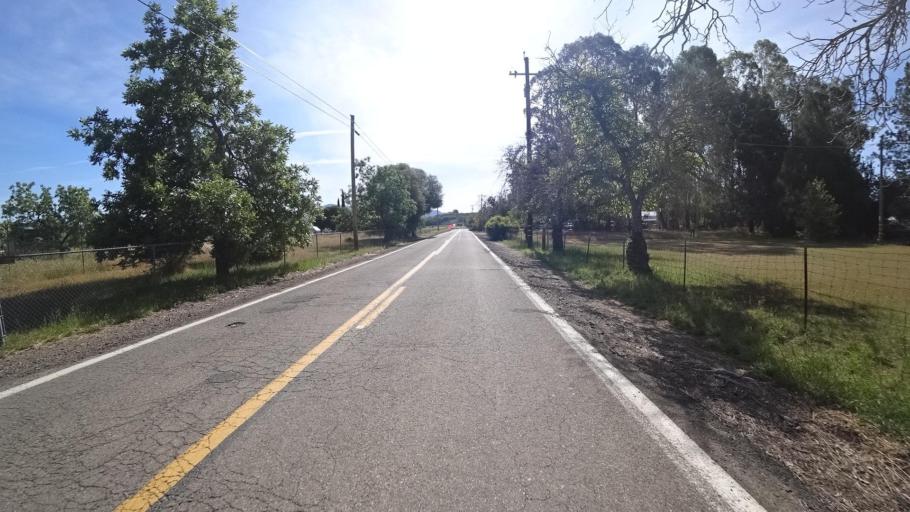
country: US
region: California
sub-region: Lake County
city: Kelseyville
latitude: 38.9573
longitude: -122.8880
